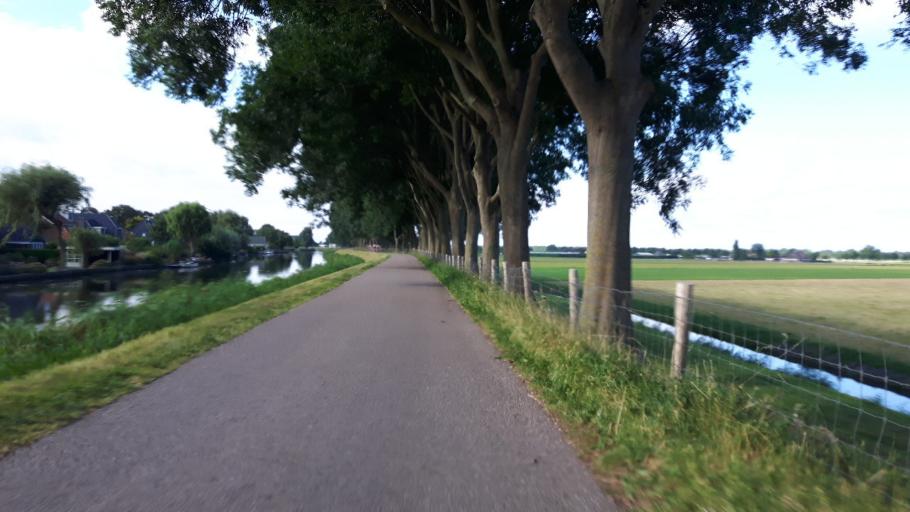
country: NL
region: North Holland
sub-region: Gemeente Purmerend
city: Purmerend
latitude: 52.5671
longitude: 4.9850
